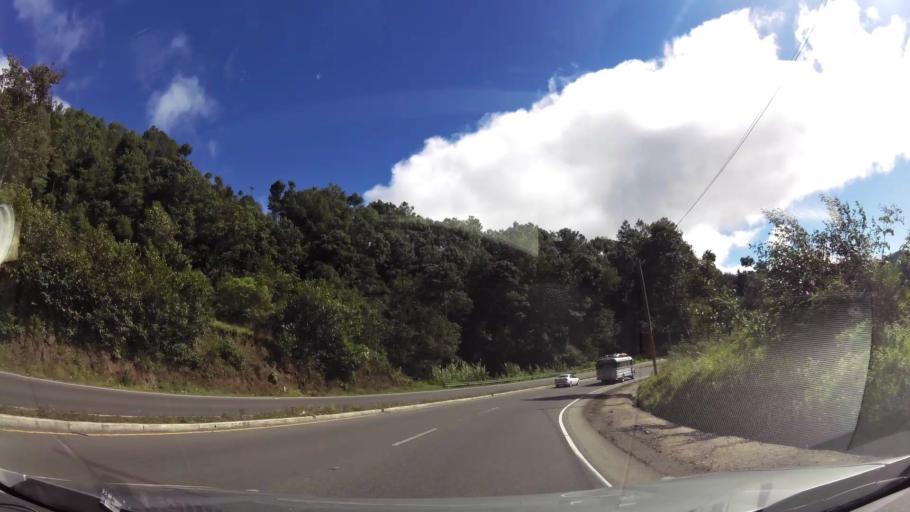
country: GT
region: Solola
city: Concepcion
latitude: 14.8377
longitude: -91.1803
